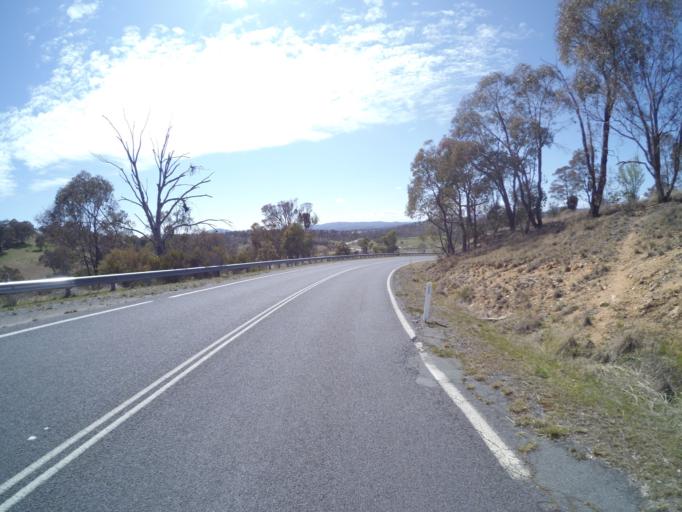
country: AU
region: Australian Capital Territory
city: Macarthur
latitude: -35.4584
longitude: 149.0370
